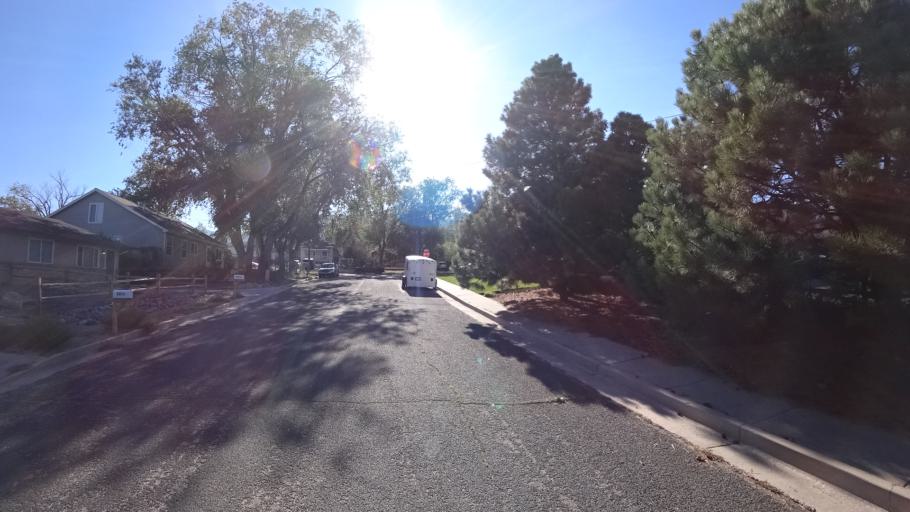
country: US
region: Colorado
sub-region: El Paso County
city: Colorado Springs
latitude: 38.8397
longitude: -104.8700
